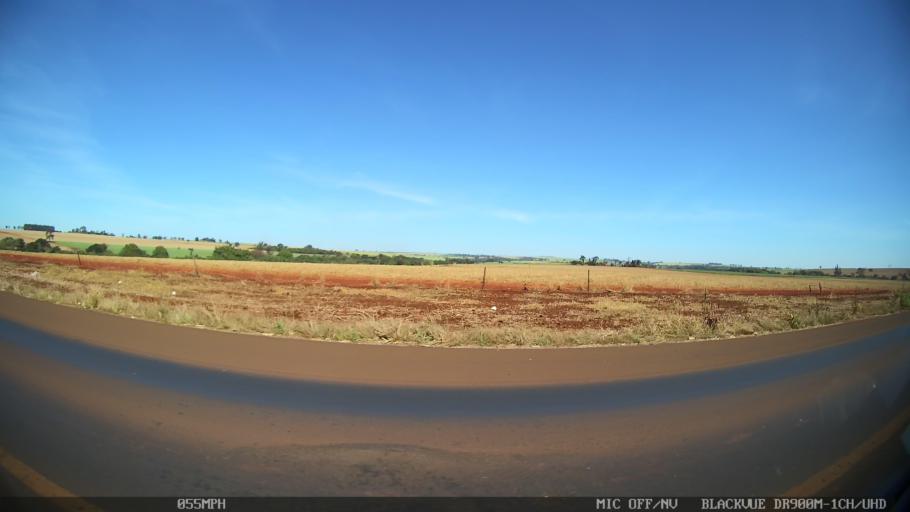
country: BR
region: Sao Paulo
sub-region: Sao Joaquim Da Barra
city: Sao Joaquim da Barra
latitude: -20.5153
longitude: -47.8876
